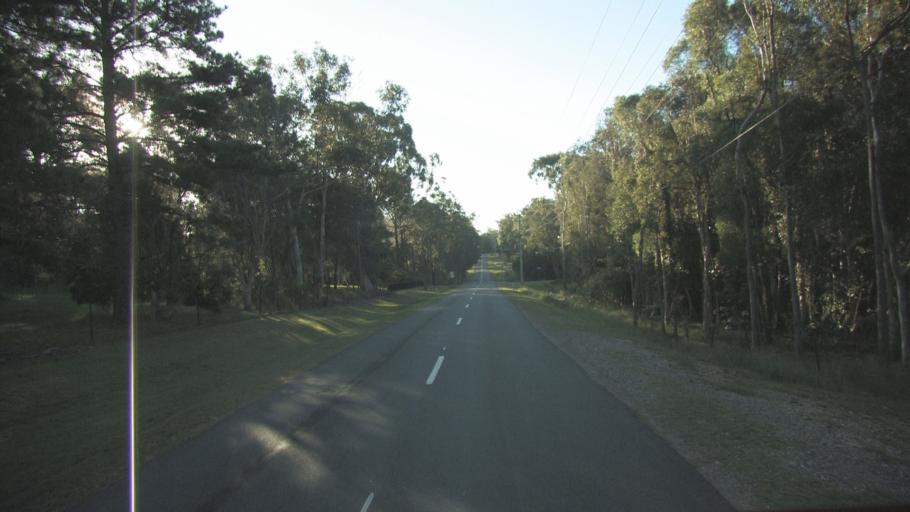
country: AU
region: Queensland
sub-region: Redland
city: Redland Bay
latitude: -27.6722
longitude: 153.2759
